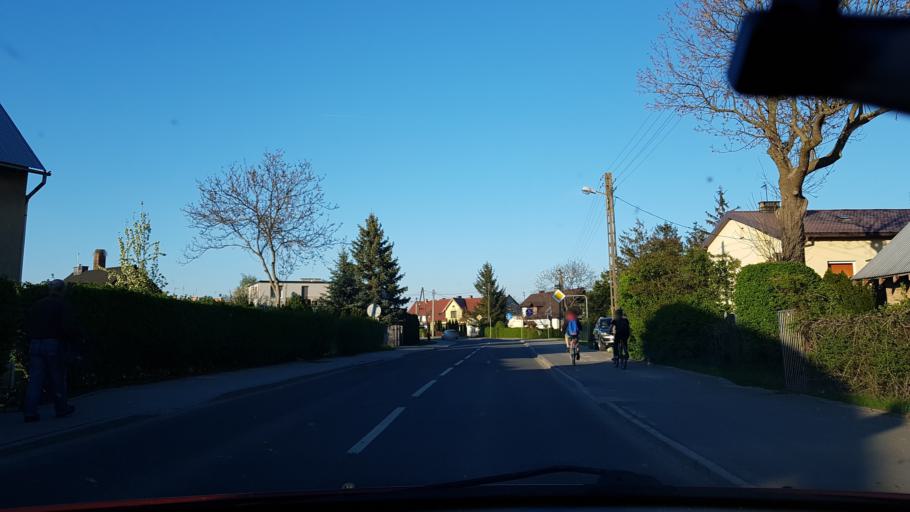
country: PL
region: Opole Voivodeship
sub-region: Powiat nyski
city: Nysa
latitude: 50.4360
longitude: 17.3063
